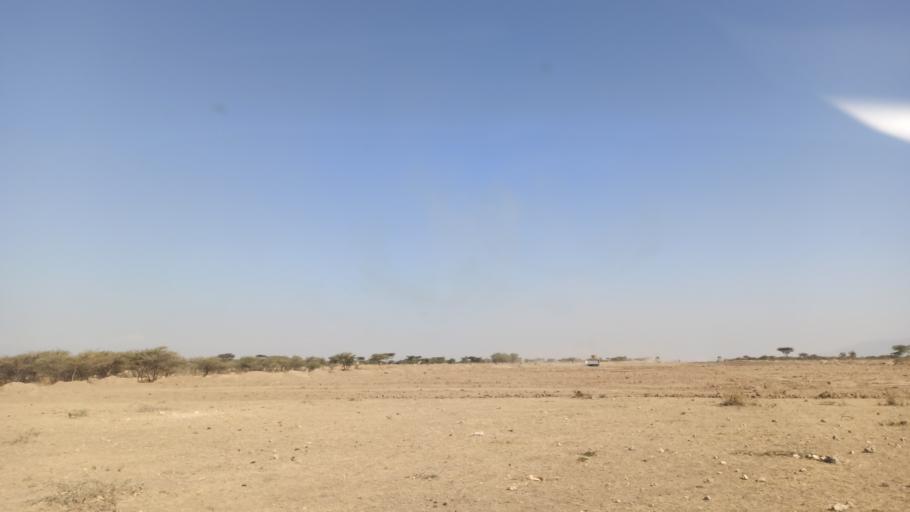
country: ET
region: Oromiya
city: Shashemene
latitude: 7.5473
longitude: 38.6728
